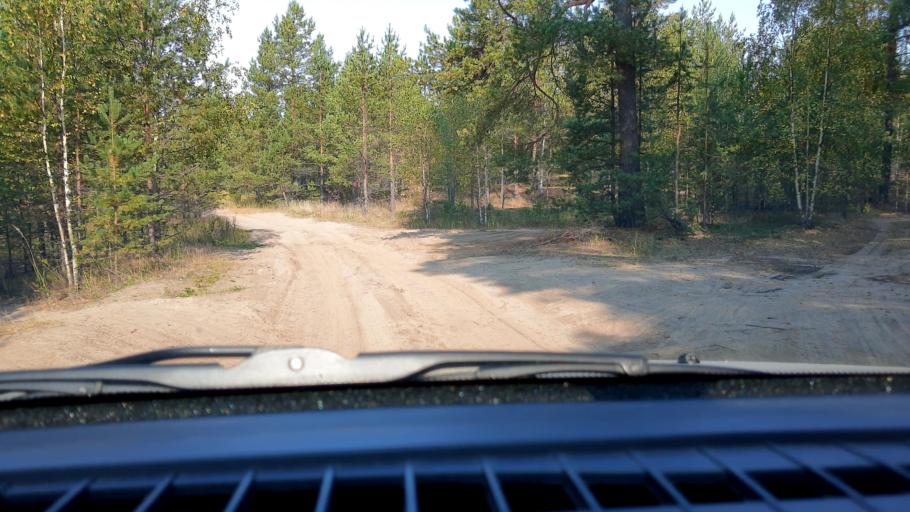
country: RU
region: Nizjnij Novgorod
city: Lukino
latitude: 56.3933
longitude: 43.6248
